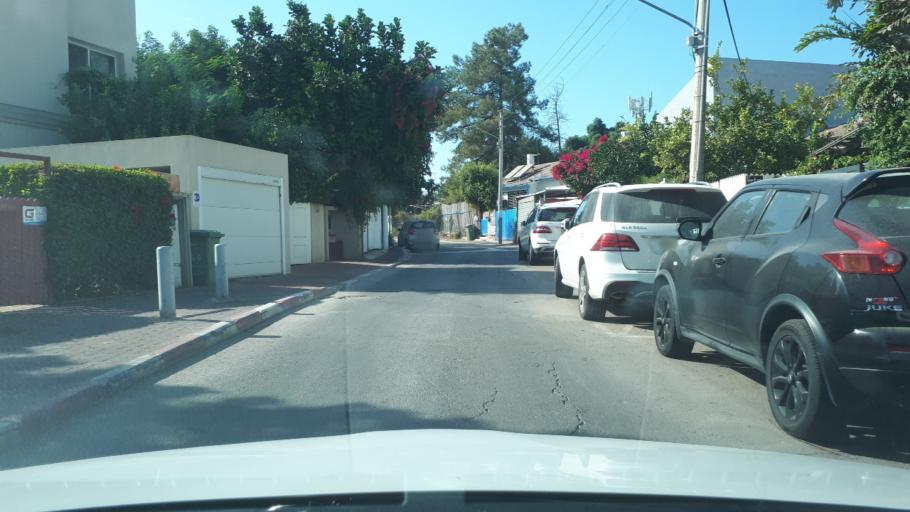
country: IL
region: Tel Aviv
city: Giv`atayim
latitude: 32.0583
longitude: 34.8263
